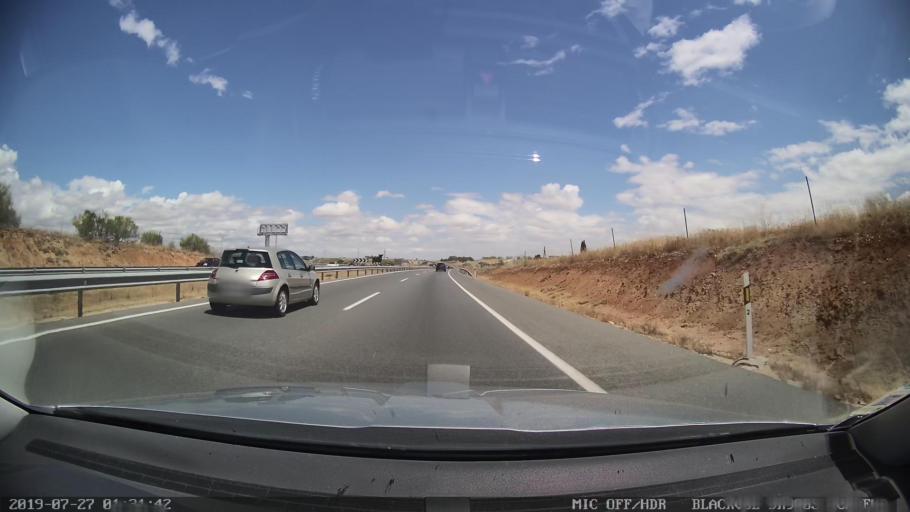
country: ES
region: Castille-La Mancha
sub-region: Province of Toledo
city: Valmojado
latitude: 40.2144
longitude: -4.0923
